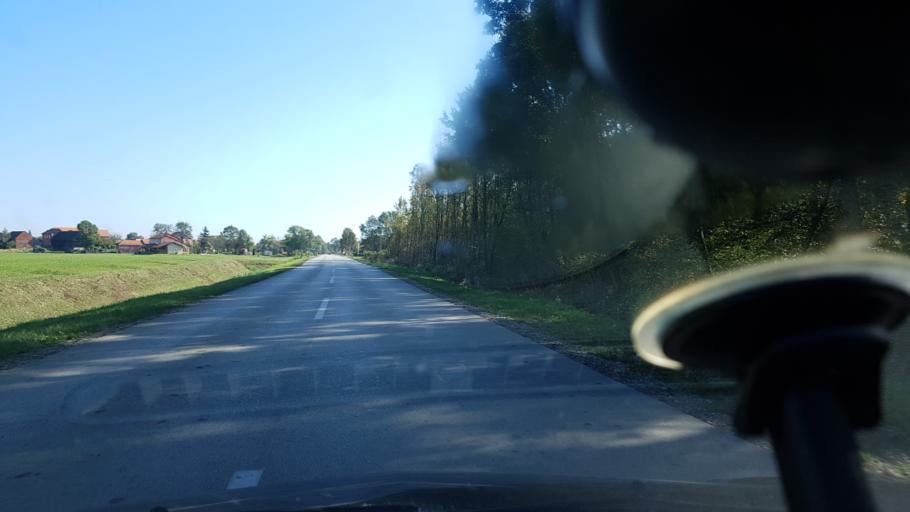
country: HR
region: Zagrebacka
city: Brckovljani
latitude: 45.7606
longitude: 16.2531
